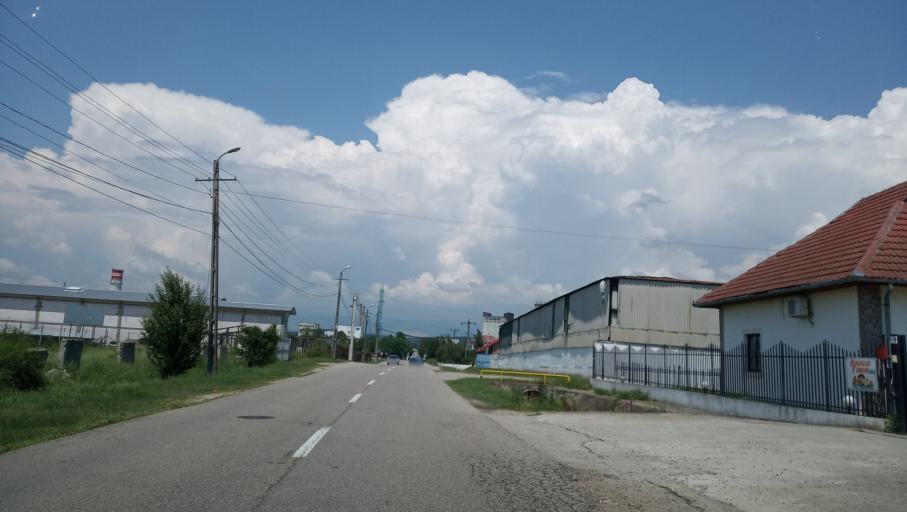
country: RO
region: Gorj
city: Targu Jiu
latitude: 45.0669
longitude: 23.3127
